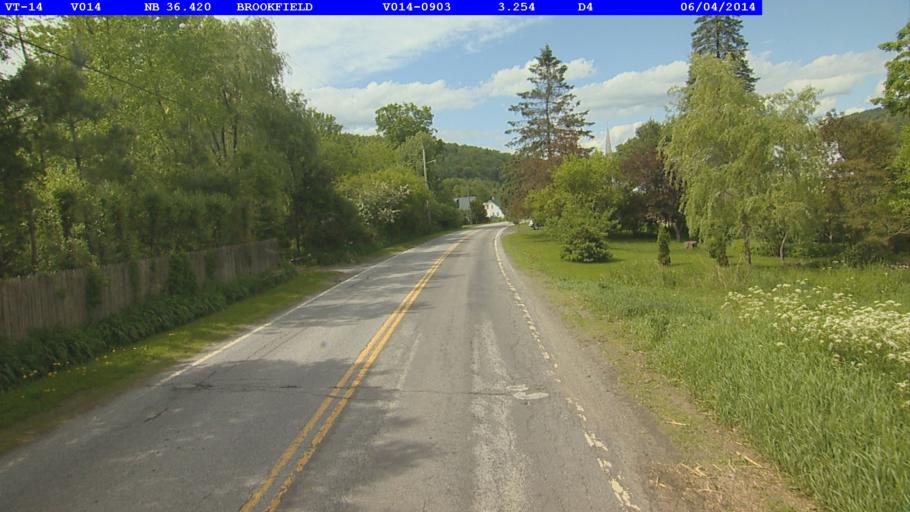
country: US
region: Vermont
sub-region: Orange County
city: Williamstown
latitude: 44.0239
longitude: -72.5713
